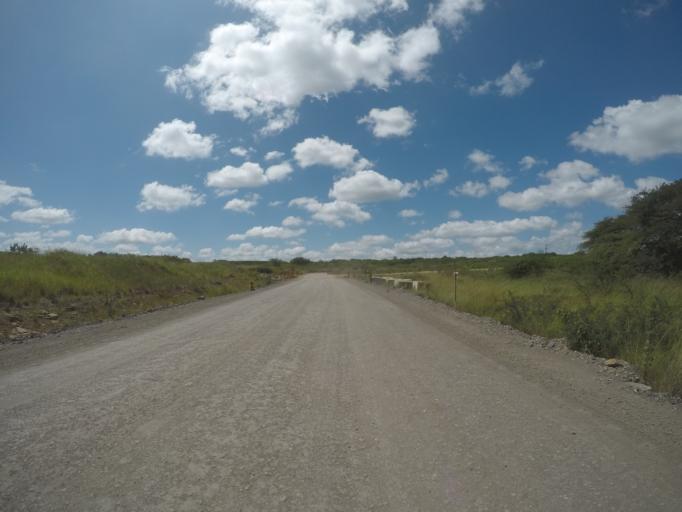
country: ZA
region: KwaZulu-Natal
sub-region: uThungulu District Municipality
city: Empangeni
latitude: -28.6614
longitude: 31.7805
